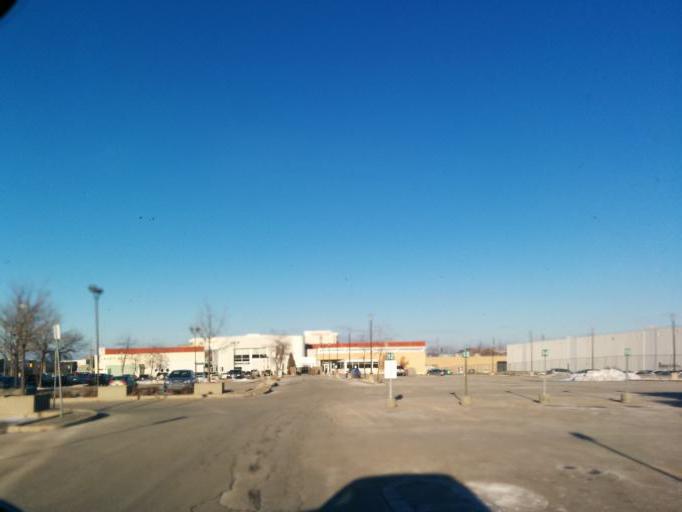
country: CA
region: Ontario
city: Etobicoke
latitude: 43.6494
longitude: -79.6038
